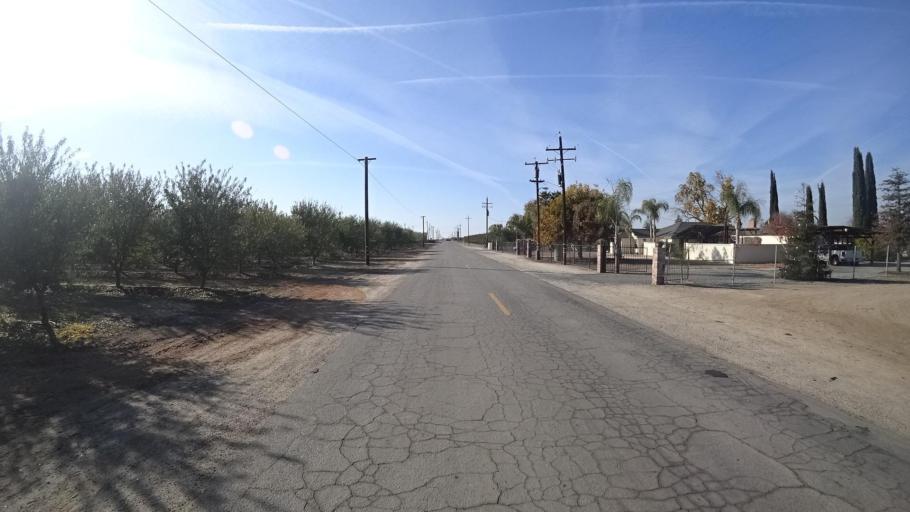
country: US
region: California
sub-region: Kern County
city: McFarland
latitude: 35.7032
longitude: -119.3269
